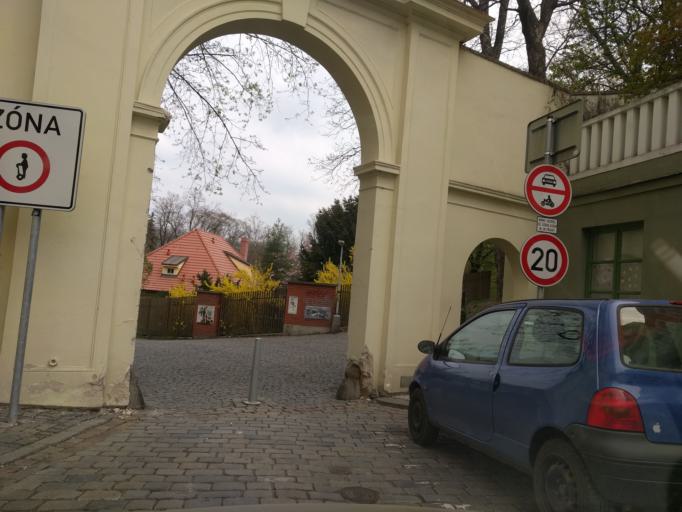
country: CZ
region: Praha
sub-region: Praha 1
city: Mala Strana
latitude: 50.1044
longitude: 14.4096
